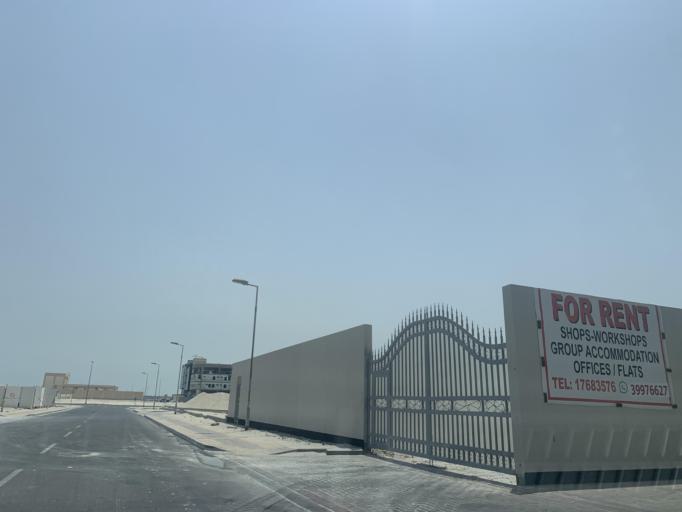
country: BH
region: Muharraq
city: Al Hadd
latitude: 26.2575
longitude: 50.6711
